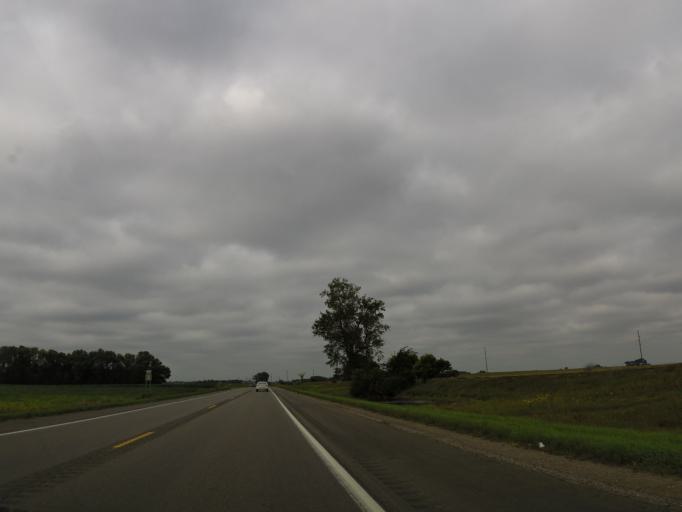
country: US
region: Minnesota
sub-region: Renville County
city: Olivia
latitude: 44.7870
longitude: -95.0606
